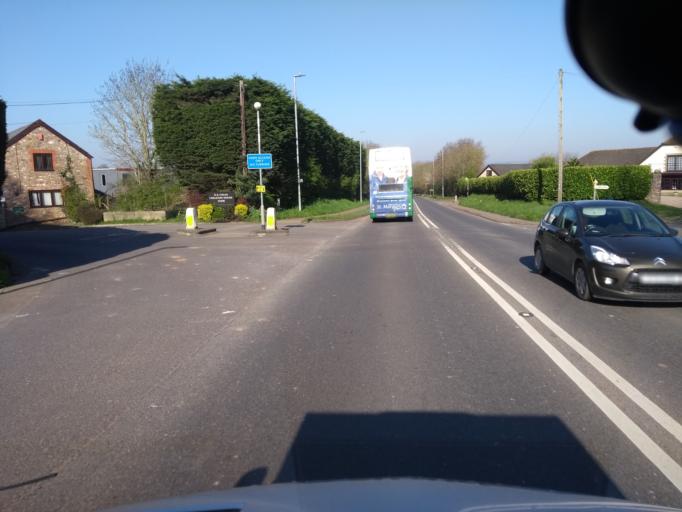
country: GB
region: England
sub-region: Somerset
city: Bishops Lydeard
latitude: 50.9825
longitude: -3.2065
